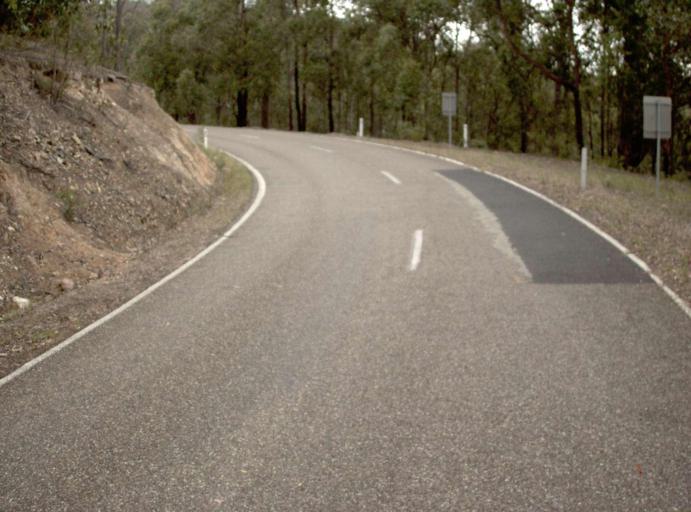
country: AU
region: Victoria
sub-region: East Gippsland
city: Bairnsdale
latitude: -37.6597
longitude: 147.2802
